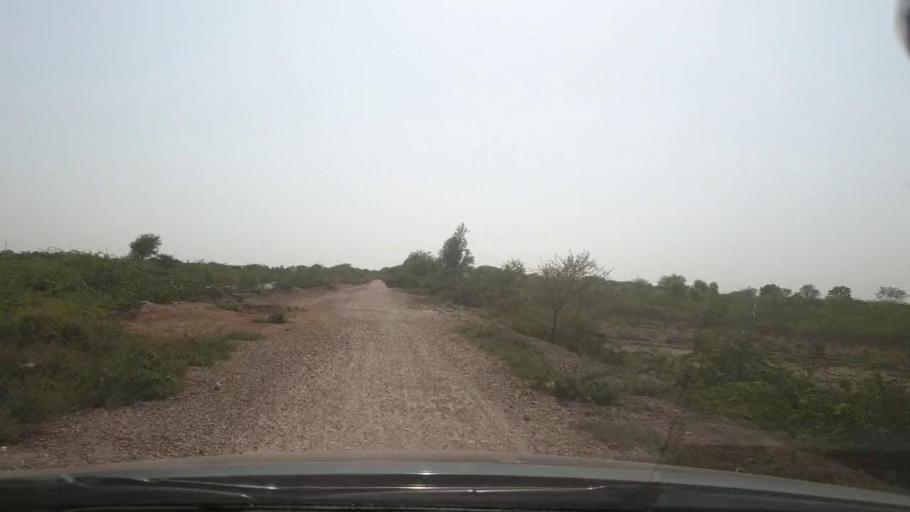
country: PK
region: Sindh
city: Naukot
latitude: 24.7861
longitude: 69.2017
